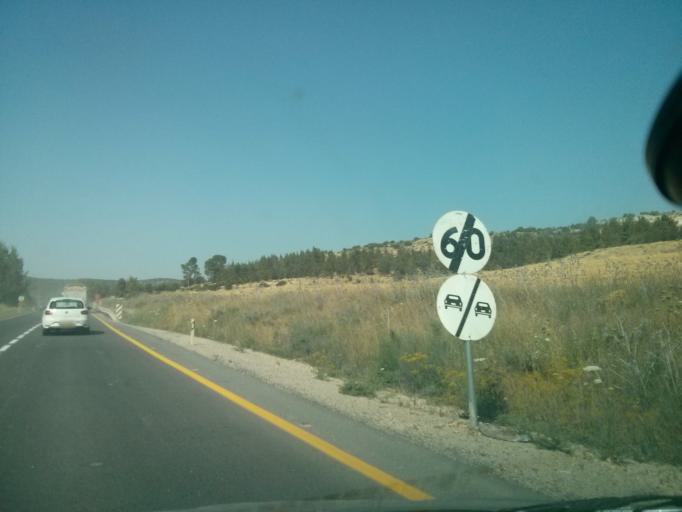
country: IL
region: Jerusalem
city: Bet Shemesh
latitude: 31.6924
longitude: 35.0088
